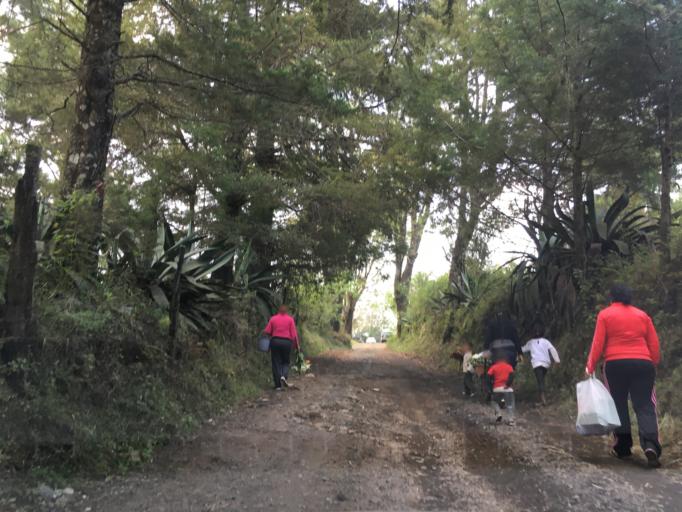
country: MX
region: Michoacan
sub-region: Uruapan
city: Santa Ana Zirosto
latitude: 19.5703
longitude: -102.2887
